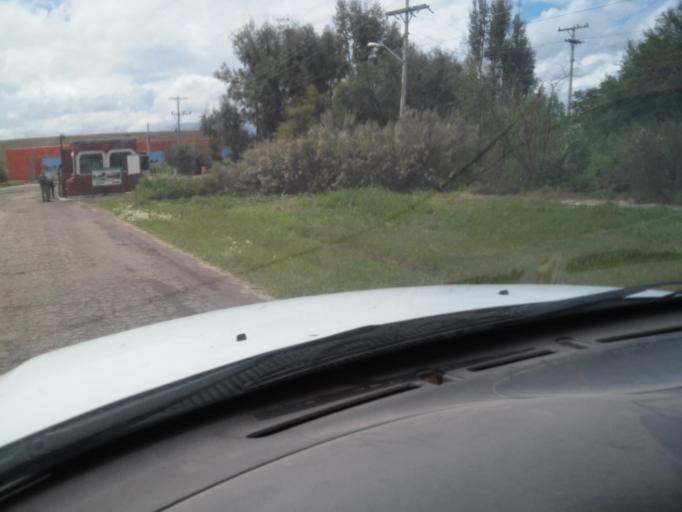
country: MX
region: Durango
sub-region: Durango
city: Jose Refugio Salcido
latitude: 24.0185
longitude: -104.5467
